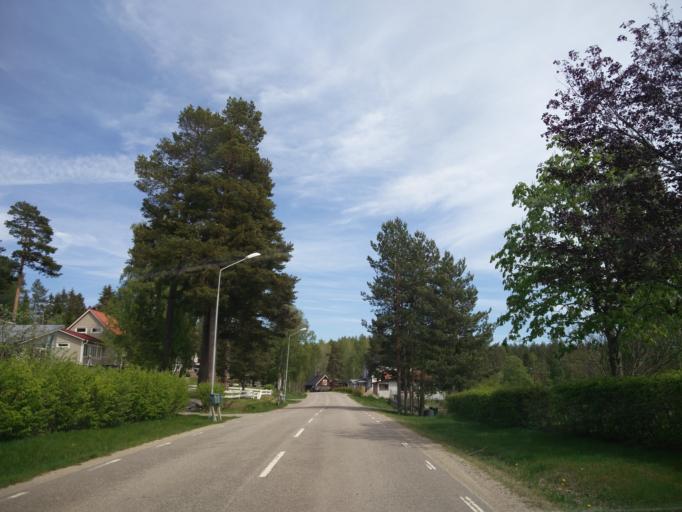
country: SE
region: Gaevleborg
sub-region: Hudiksvalls Kommun
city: Sorforsa
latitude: 61.7102
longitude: 16.9532
